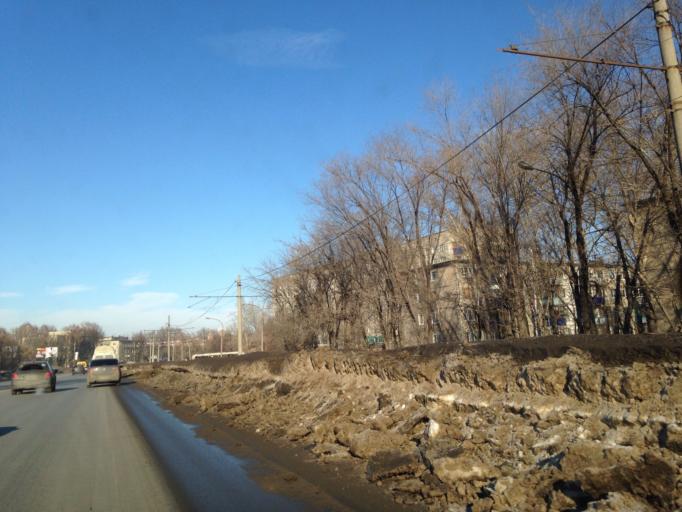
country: RU
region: Ulyanovsk
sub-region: Ulyanovskiy Rayon
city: Ulyanovsk
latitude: 54.3087
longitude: 48.3502
